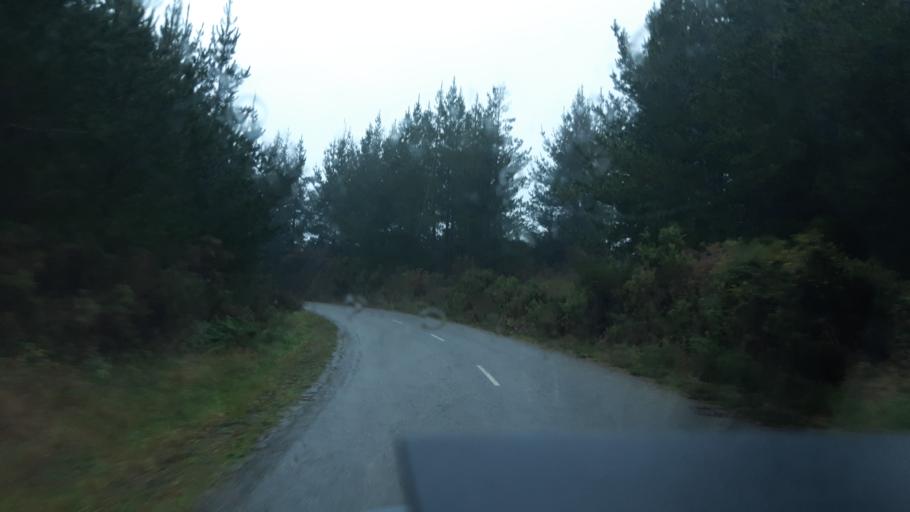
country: NZ
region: Tasman
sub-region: Tasman District
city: Wakefield
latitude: -41.5076
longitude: 172.9558
